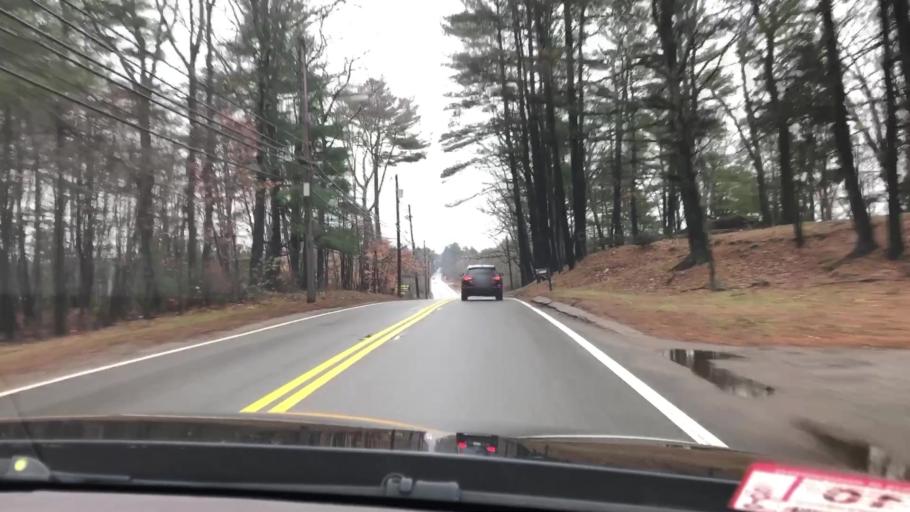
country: US
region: Massachusetts
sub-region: Norfolk County
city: Walpole
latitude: 42.1191
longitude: -71.2767
